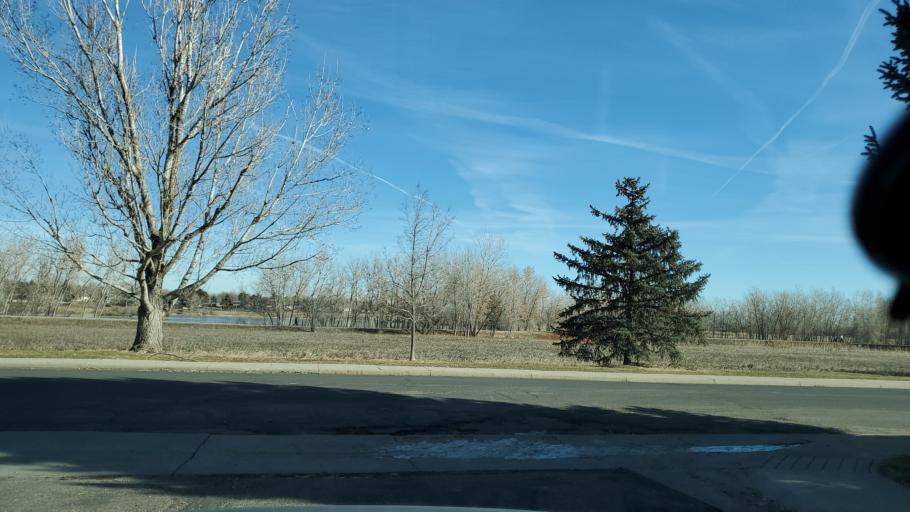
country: US
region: Colorado
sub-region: Adams County
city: Northglenn
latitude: 39.9244
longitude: -104.9544
